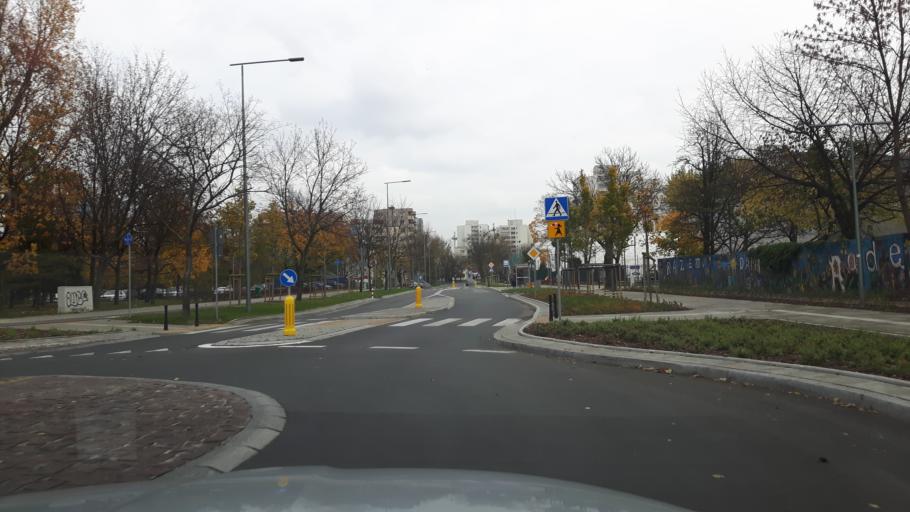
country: PL
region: Masovian Voivodeship
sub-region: Warszawa
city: Targowek
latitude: 52.2735
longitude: 21.0531
